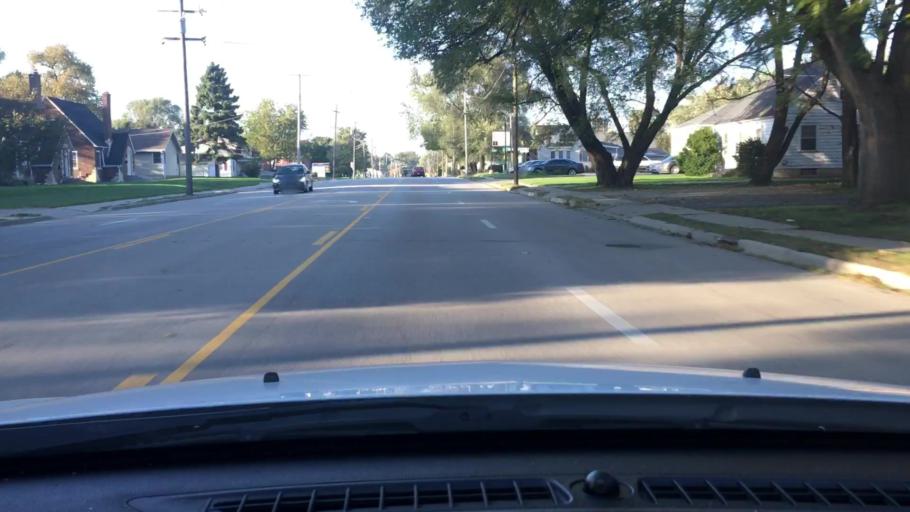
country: US
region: Illinois
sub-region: DeKalb County
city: DeKalb
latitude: 41.9158
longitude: -88.7534
